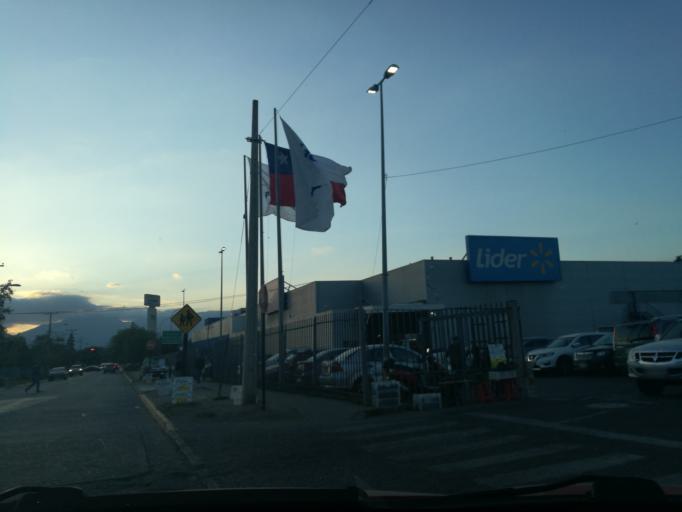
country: CL
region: O'Higgins
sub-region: Provincia de Cachapoal
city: Rancagua
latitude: -34.1600
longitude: -70.7370
